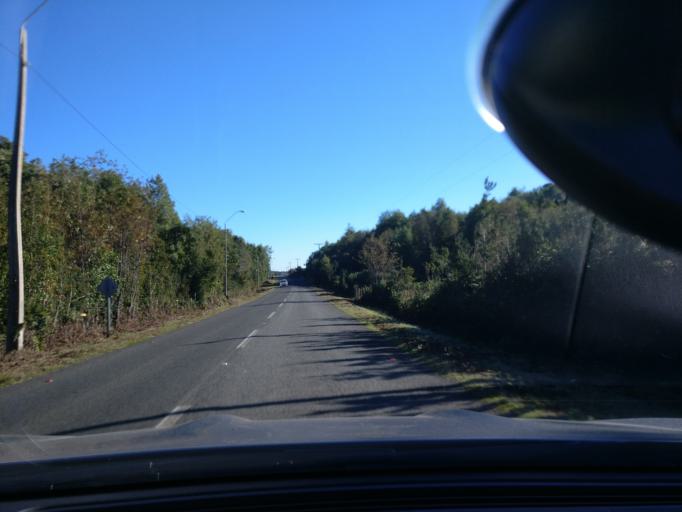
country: CL
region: Los Lagos
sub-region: Provincia de Chiloe
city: Castro
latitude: -42.3177
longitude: -73.3776
